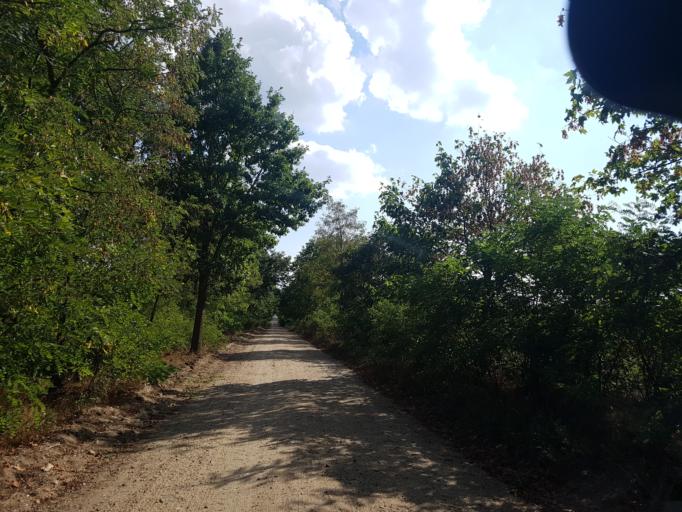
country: DE
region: Brandenburg
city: Gorzke
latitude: 52.0423
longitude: 12.2941
